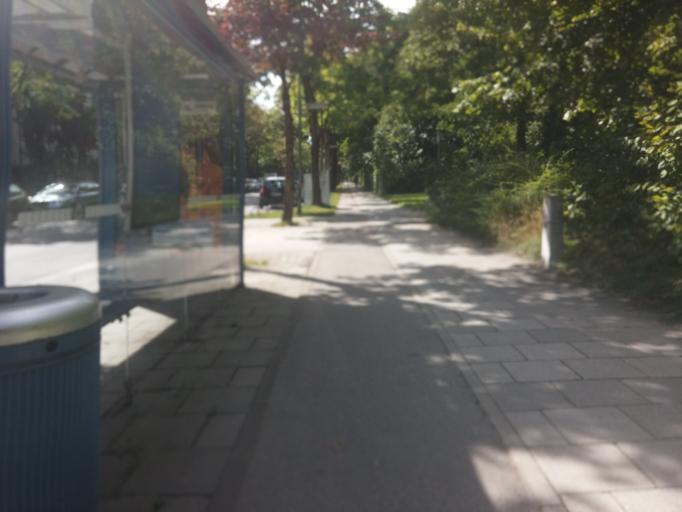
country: DE
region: Bavaria
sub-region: Upper Bavaria
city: Bogenhausen
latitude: 48.1514
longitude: 11.6263
